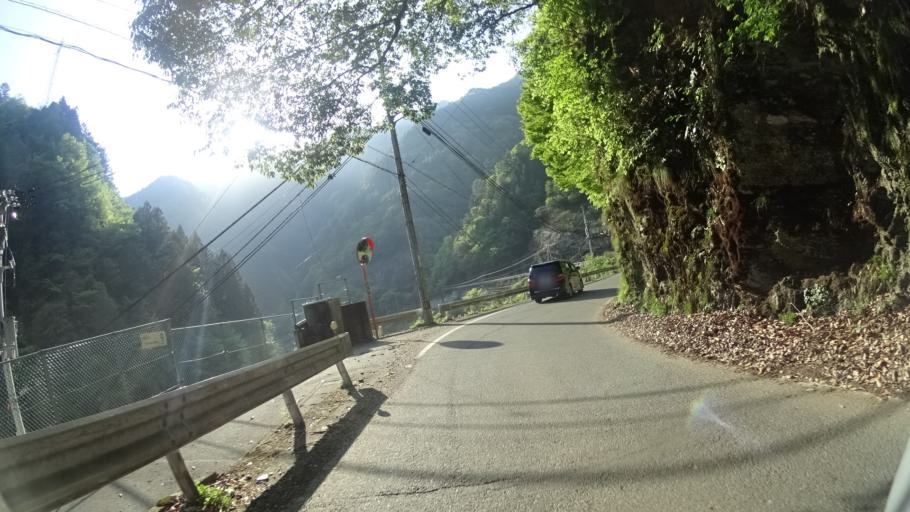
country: JP
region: Tokushima
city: Ikedacho
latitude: 33.8919
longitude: 133.8508
